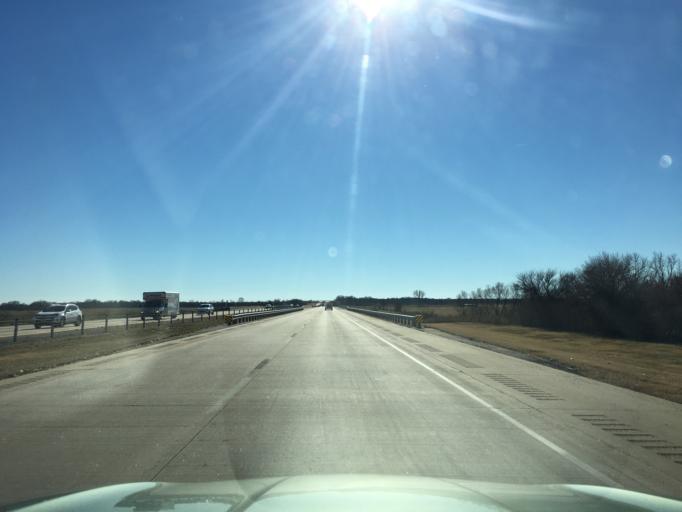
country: US
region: Oklahoma
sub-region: Noble County
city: Perry
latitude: 36.4725
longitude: -97.3271
